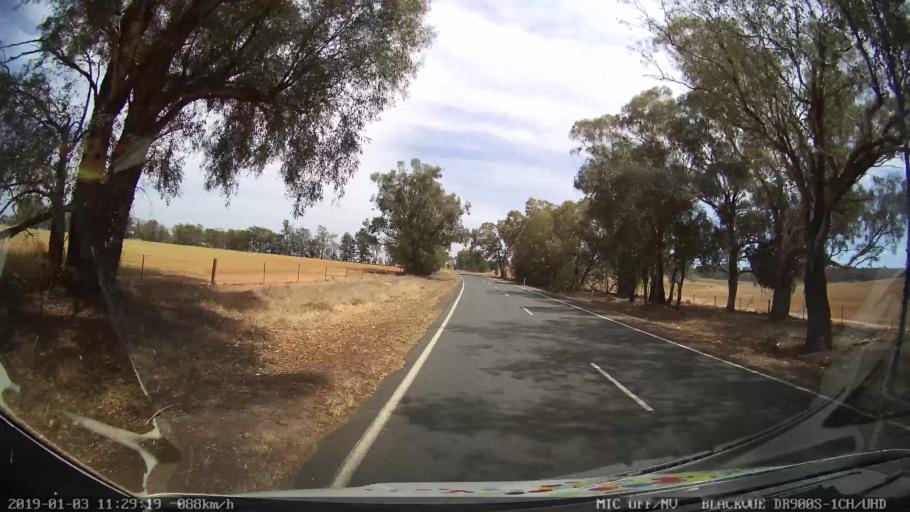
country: AU
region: New South Wales
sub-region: Weddin
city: Grenfell
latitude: -33.9935
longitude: 148.1997
